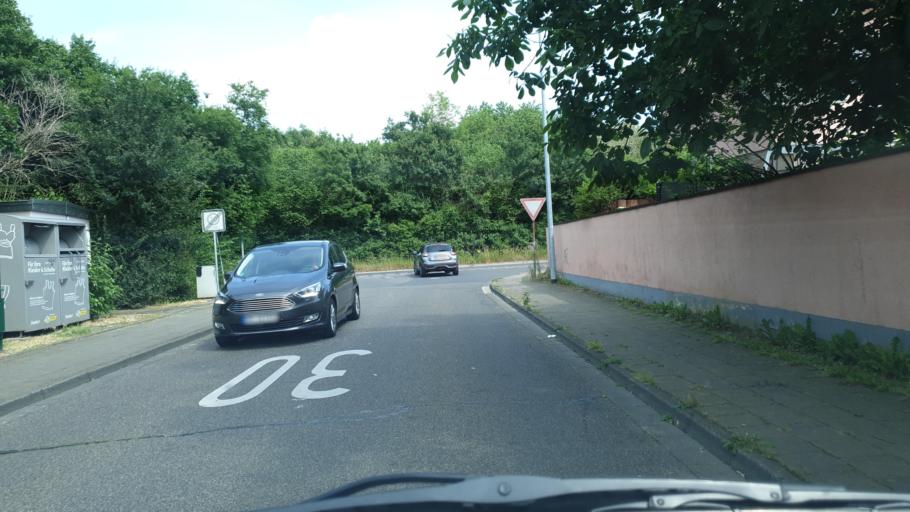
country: DE
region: North Rhine-Westphalia
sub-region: Regierungsbezirk Koln
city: Bergheim
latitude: 50.9390
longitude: 6.6686
